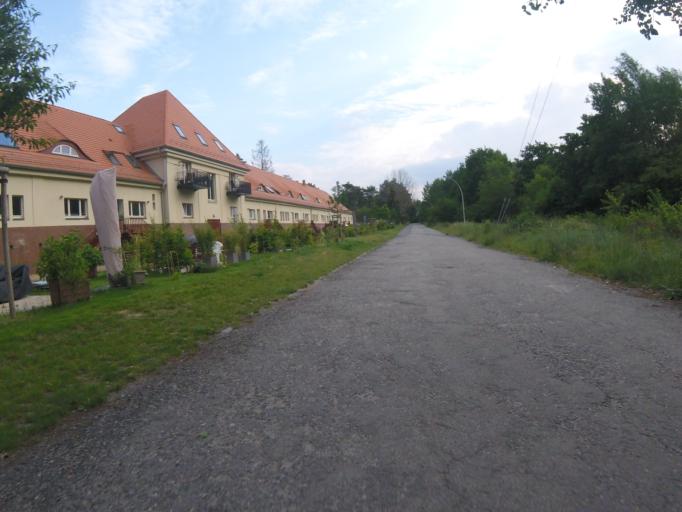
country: DE
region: Brandenburg
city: Konigs Wusterhausen
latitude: 52.3045
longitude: 13.6173
